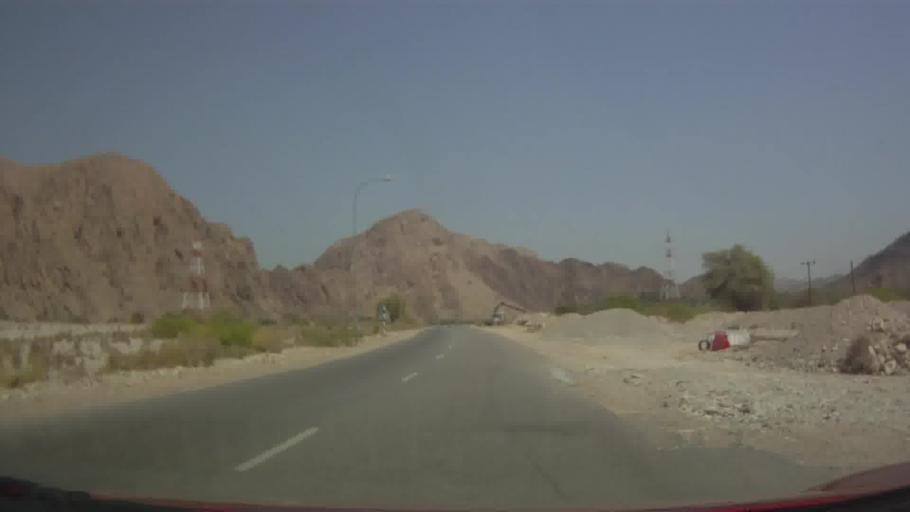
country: OM
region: Muhafazat Masqat
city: Muscat
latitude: 23.5096
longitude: 58.6399
